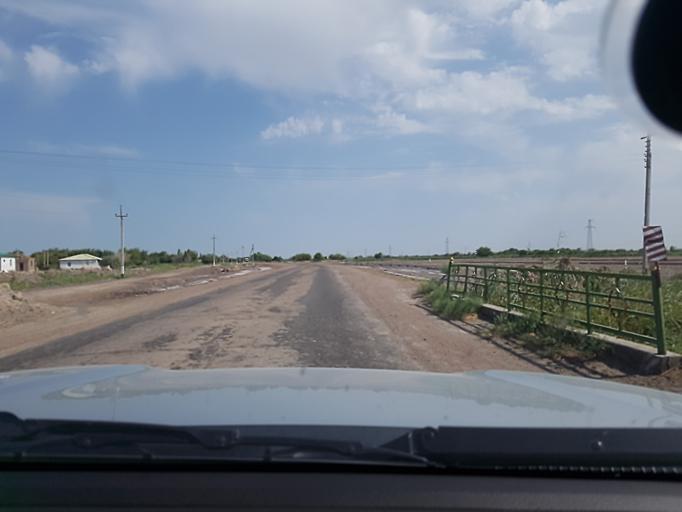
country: TM
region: Dasoguz
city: Boldumsaz
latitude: 42.0965
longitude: 59.7119
